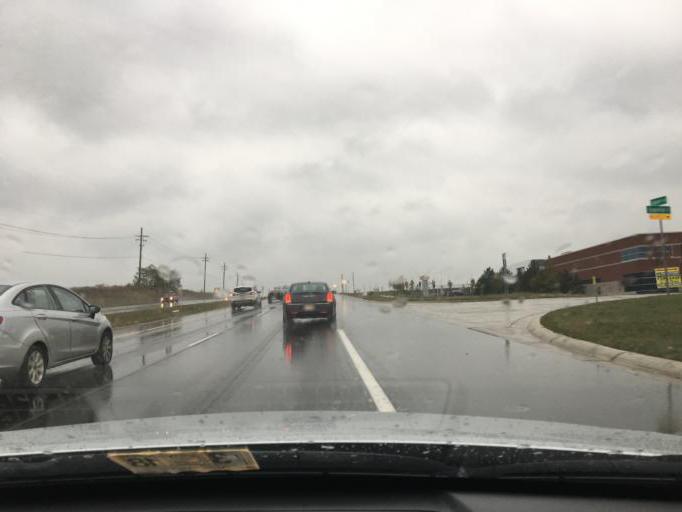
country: US
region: Michigan
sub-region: Oakland County
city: Auburn Hills
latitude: 42.7034
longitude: -83.2423
